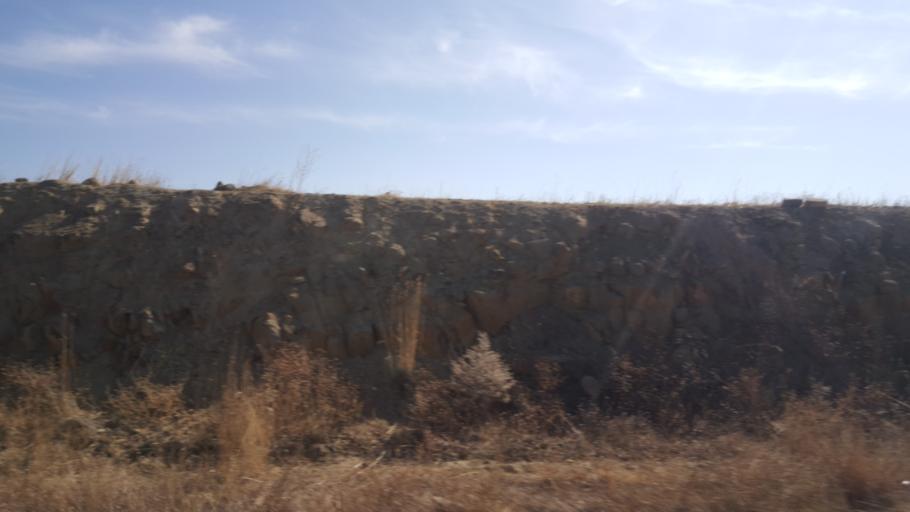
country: TR
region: Ankara
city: Yenice
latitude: 39.3650
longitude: 32.6861
